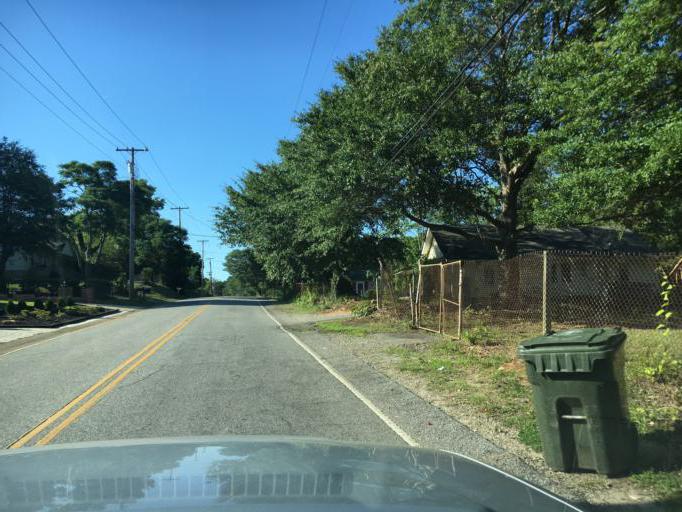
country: US
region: South Carolina
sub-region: Greenville County
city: Greer
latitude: 34.9394
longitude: -82.2157
